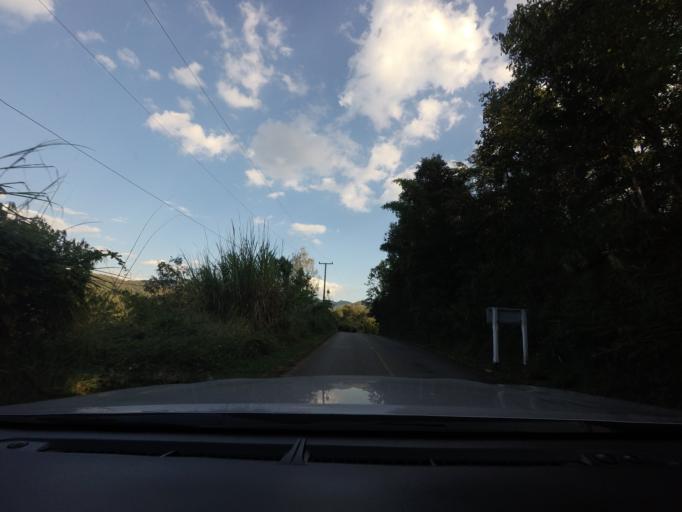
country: TH
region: Chiang Mai
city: Phrao
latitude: 19.5290
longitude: 99.1599
